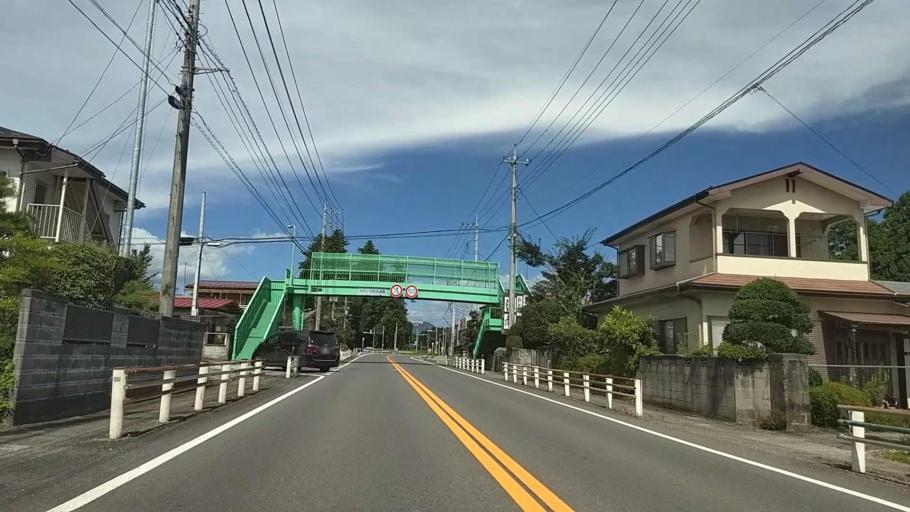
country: JP
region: Tochigi
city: Imaichi
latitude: 36.6959
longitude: 139.7563
